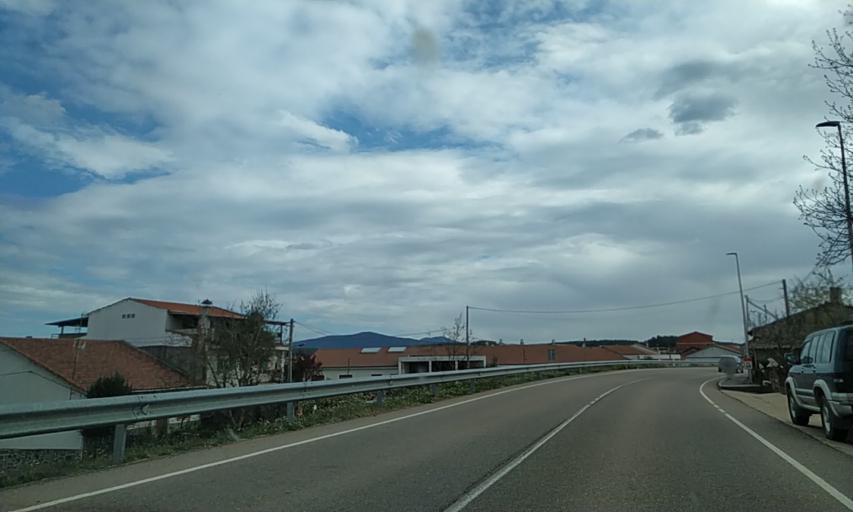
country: ES
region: Castille and Leon
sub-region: Provincia de Salamanca
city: Robleda
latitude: 40.3892
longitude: -6.6067
